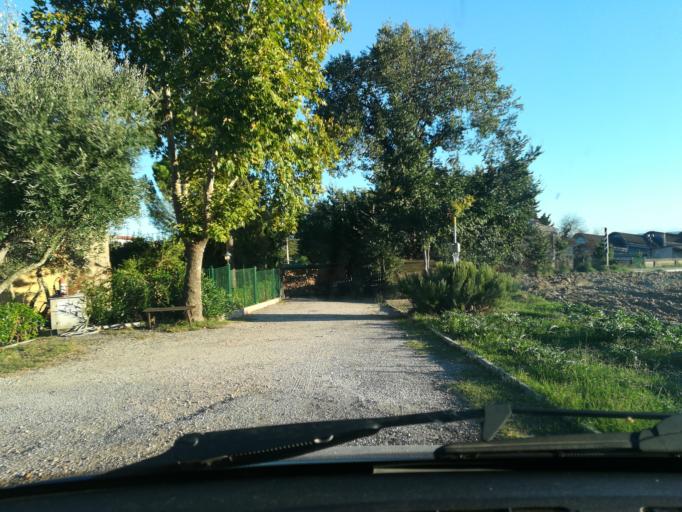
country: IT
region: The Marches
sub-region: Provincia di Macerata
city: Piediripa
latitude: 43.2836
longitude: 13.4811
